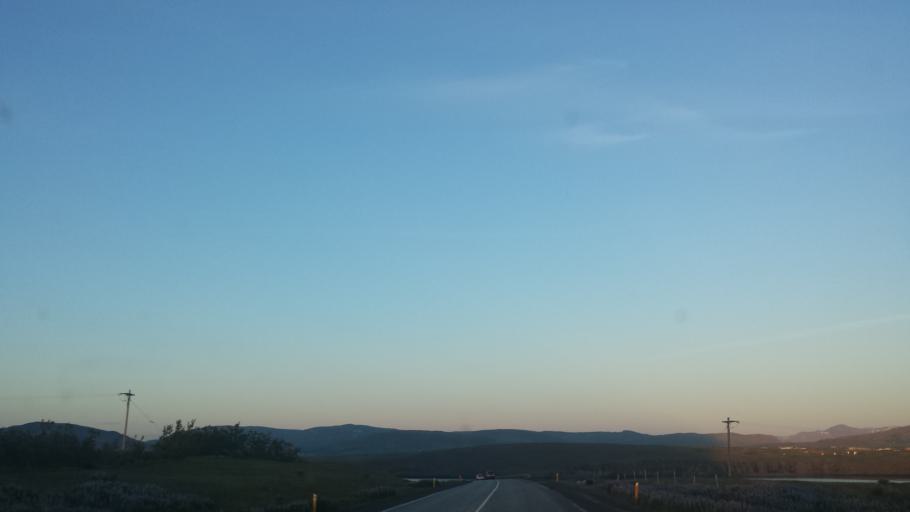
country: IS
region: Capital Region
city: Mosfellsbaer
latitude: 64.2080
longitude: -21.7618
